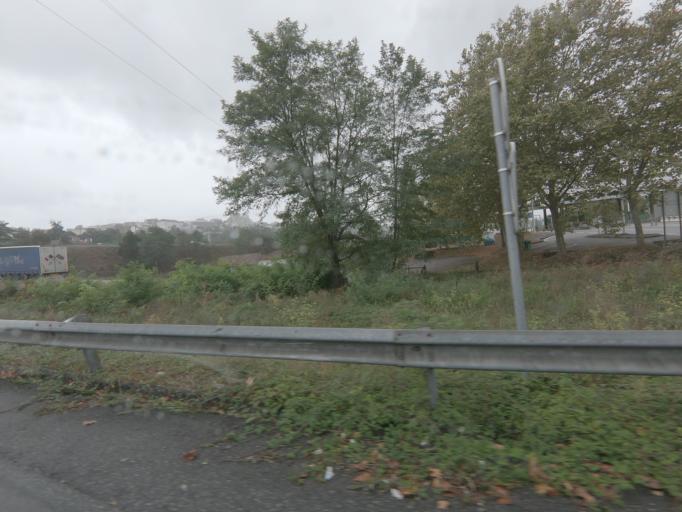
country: PT
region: Porto
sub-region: Penafiel
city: Penafiel
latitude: 41.2146
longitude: -8.2867
